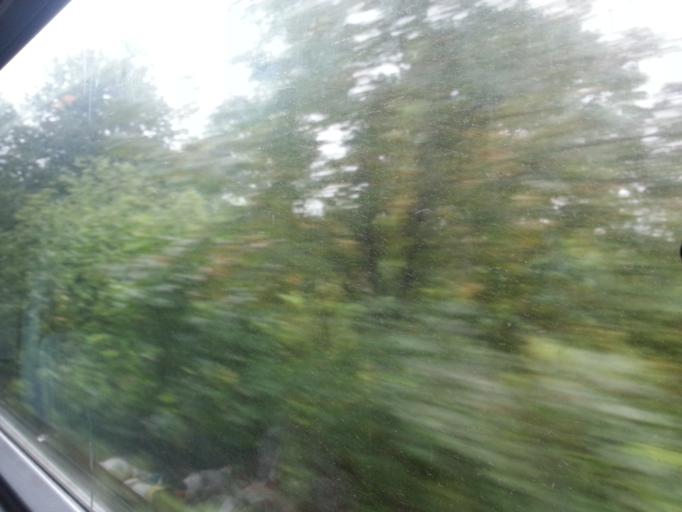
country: CA
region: British Columbia
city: Agassiz
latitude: 49.2529
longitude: -121.6818
